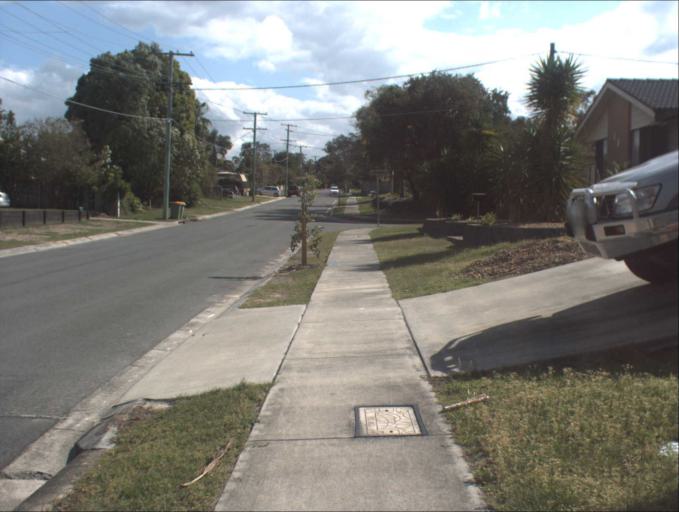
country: AU
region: Queensland
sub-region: Logan
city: Park Ridge South
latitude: -27.6905
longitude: 153.0139
